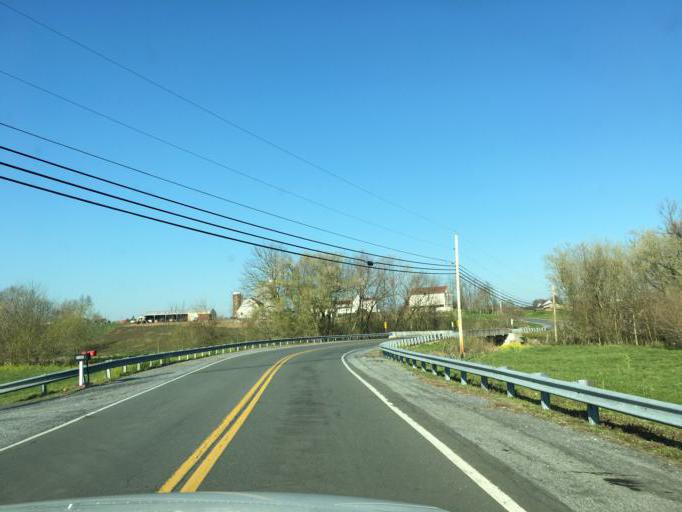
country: US
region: Maryland
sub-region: Frederick County
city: Walkersville
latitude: 39.4929
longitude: -77.3229
